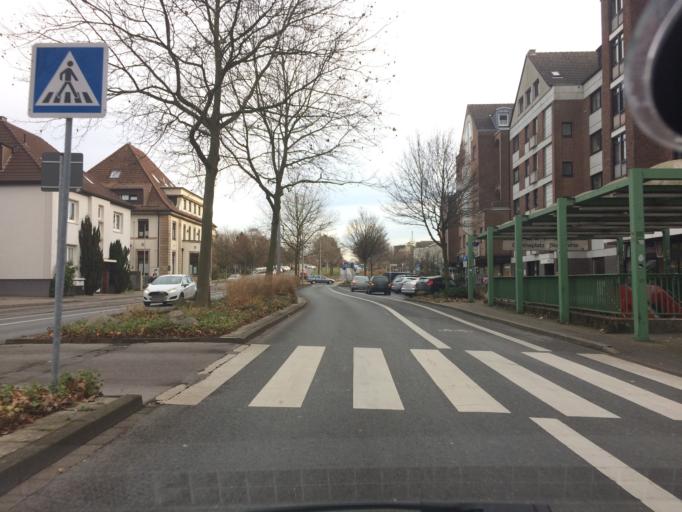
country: DE
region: North Rhine-Westphalia
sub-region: Regierungsbezirk Munster
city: Gladbeck
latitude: 51.5745
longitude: 6.9910
